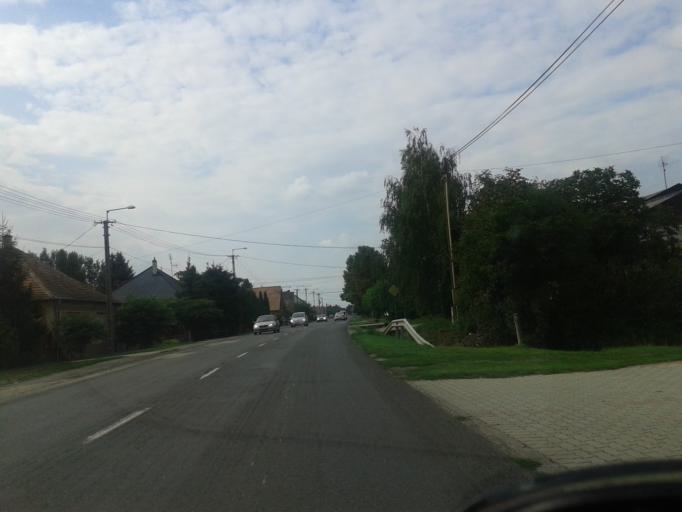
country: HU
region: Bacs-Kiskun
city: Akaszto
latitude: 46.6840
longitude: 19.2113
